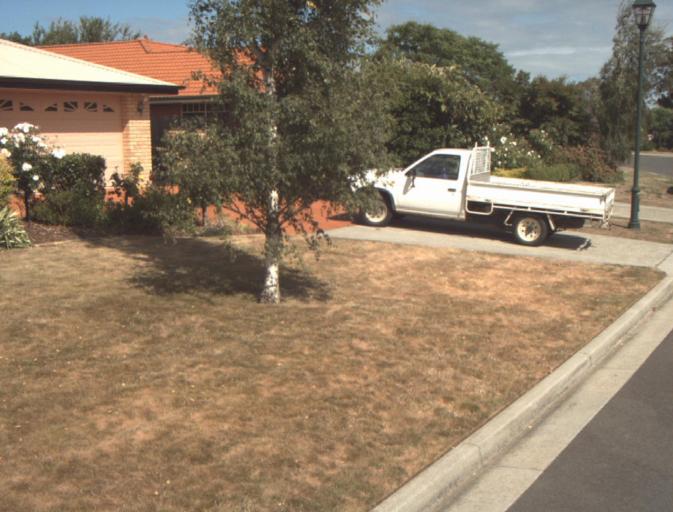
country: AU
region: Tasmania
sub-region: Launceston
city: Summerhill
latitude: -41.4741
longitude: 147.1171
